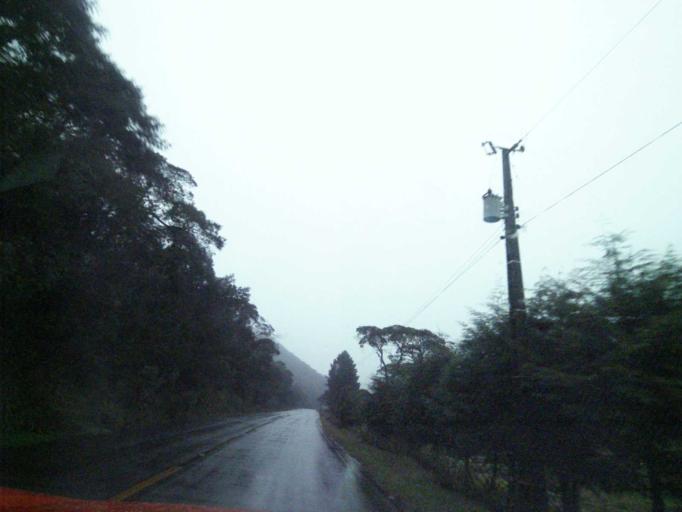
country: BR
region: Santa Catarina
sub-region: Anitapolis
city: Anitapolis
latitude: -27.7567
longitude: -49.0357
